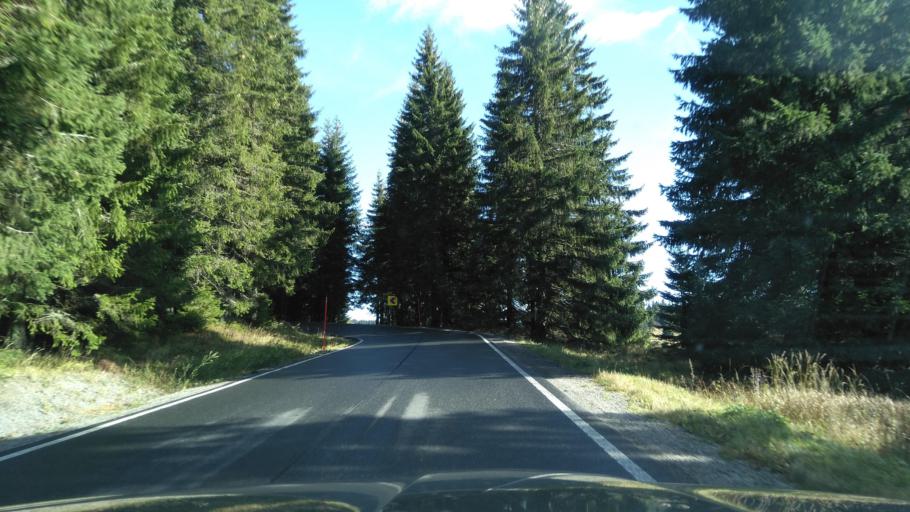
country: CZ
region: Plzensky
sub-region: Okres Klatovy
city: Kasperske Hory
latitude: 49.0242
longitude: 13.5135
